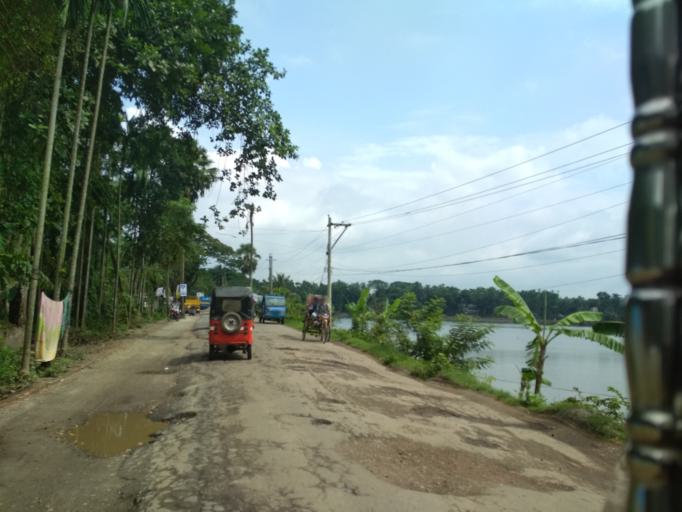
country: BD
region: Chittagong
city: Lakshmipur
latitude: 22.9662
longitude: 90.8097
